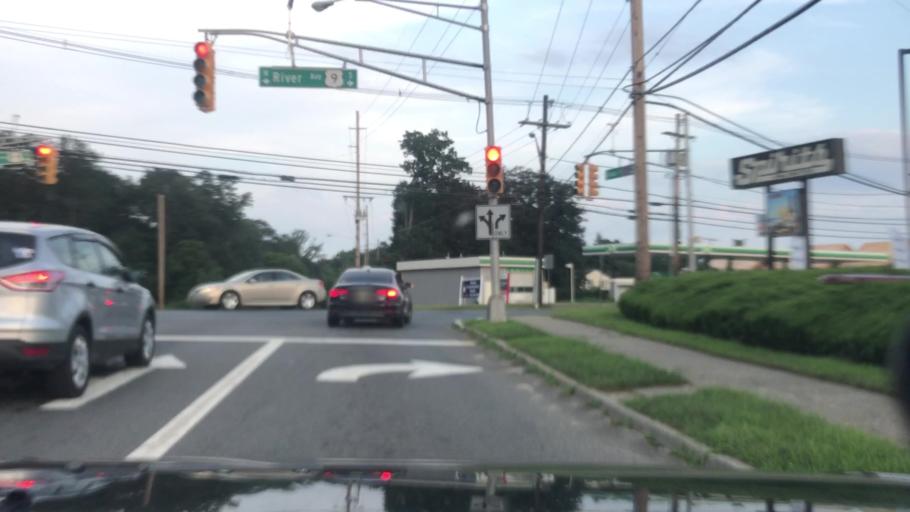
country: US
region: New Jersey
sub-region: Ocean County
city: Leisure Village
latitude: 40.0544
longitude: -74.2210
